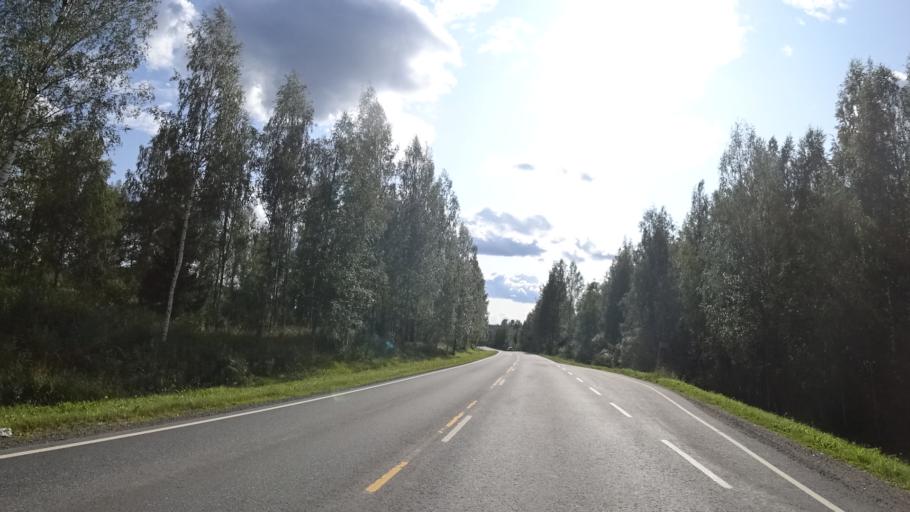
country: FI
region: North Karelia
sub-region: Keski-Karjala
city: Tohmajaervi
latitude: 62.2285
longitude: 30.3186
